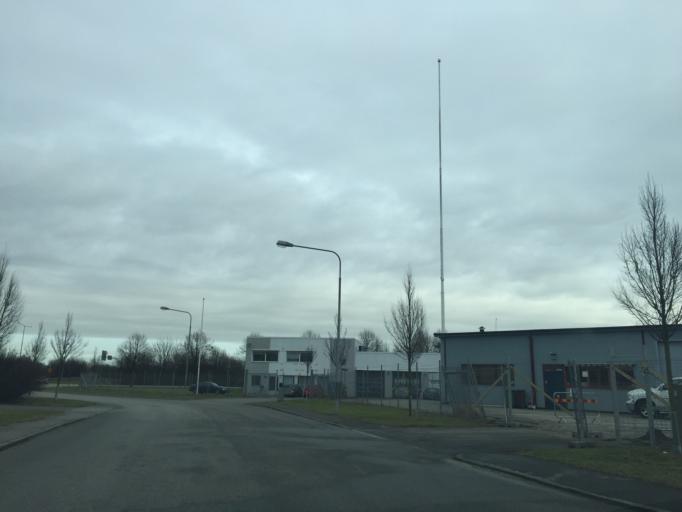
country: SE
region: Skane
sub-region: Burlovs Kommun
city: Arloev
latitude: 55.6055
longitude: 13.0654
